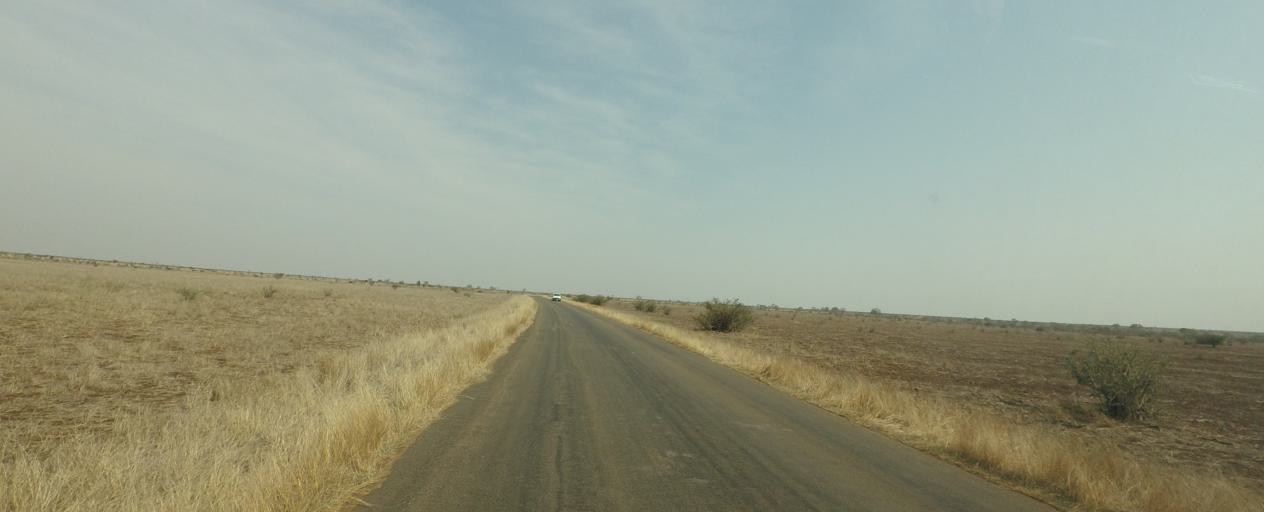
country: ZA
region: Limpopo
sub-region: Mopani District Municipality
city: Phalaborwa
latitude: -24.2739
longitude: 31.7344
